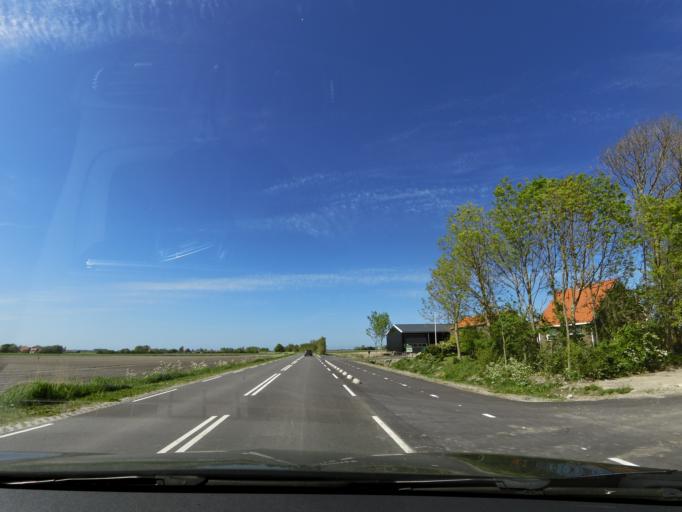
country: NL
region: Zeeland
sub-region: Schouwen-Duiveland
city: Bruinisse
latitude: 51.6535
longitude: 3.9944
